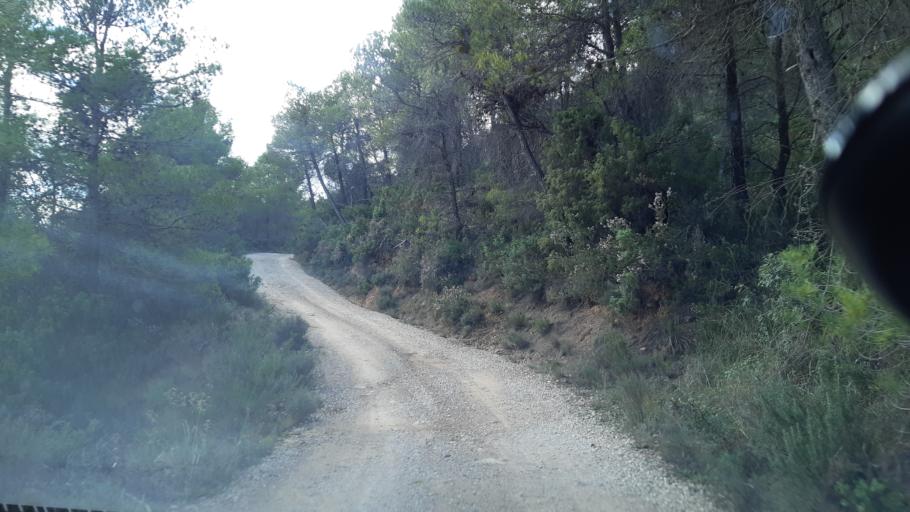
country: ES
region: Aragon
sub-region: Provincia de Teruel
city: Valderrobres
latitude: 40.8606
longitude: 0.2407
